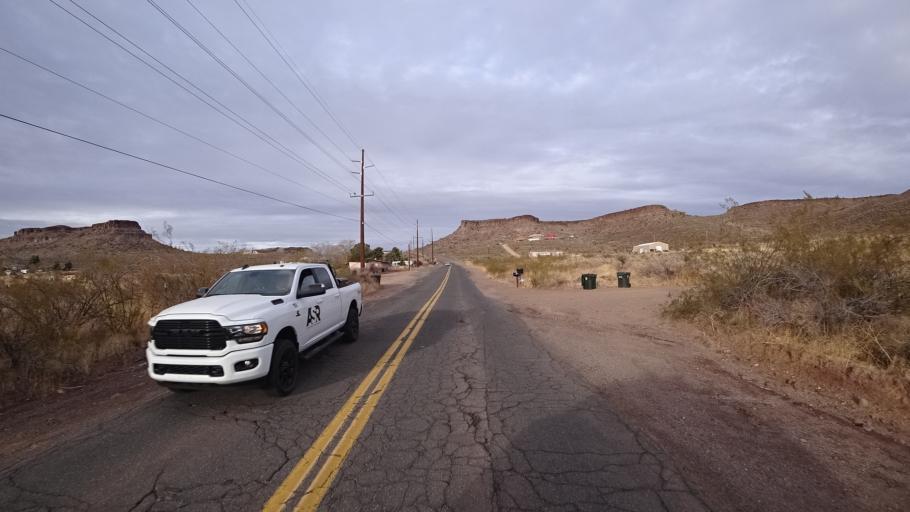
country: US
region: Arizona
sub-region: Mohave County
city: Kingman
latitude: 35.2181
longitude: -114.0558
